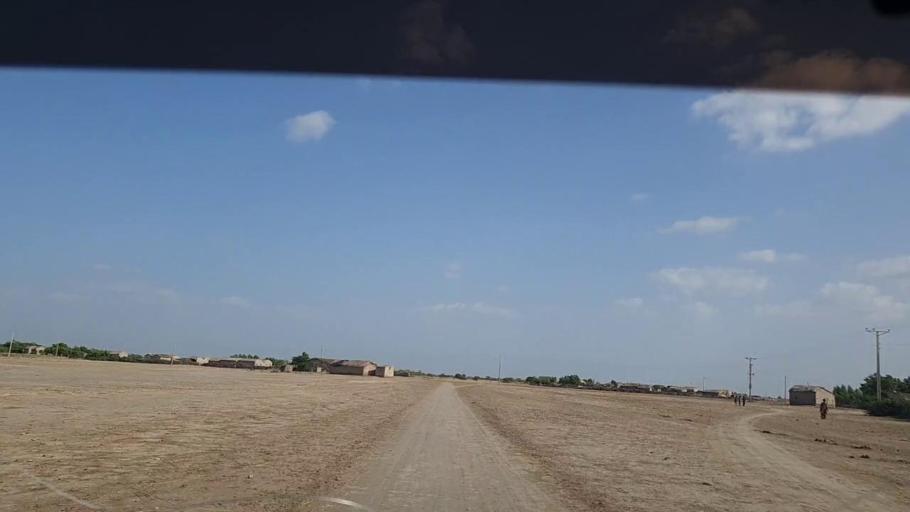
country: PK
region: Sindh
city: Kadhan
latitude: 24.4596
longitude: 68.8555
